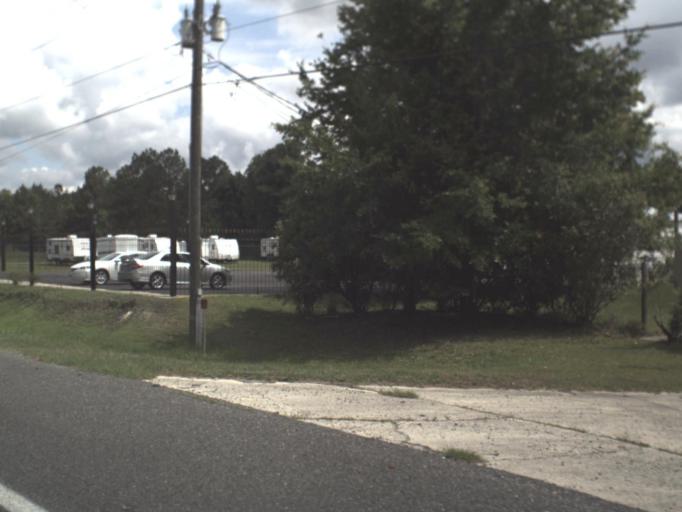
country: US
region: Florida
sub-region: Nassau County
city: Callahan
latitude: 30.5423
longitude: -81.8143
